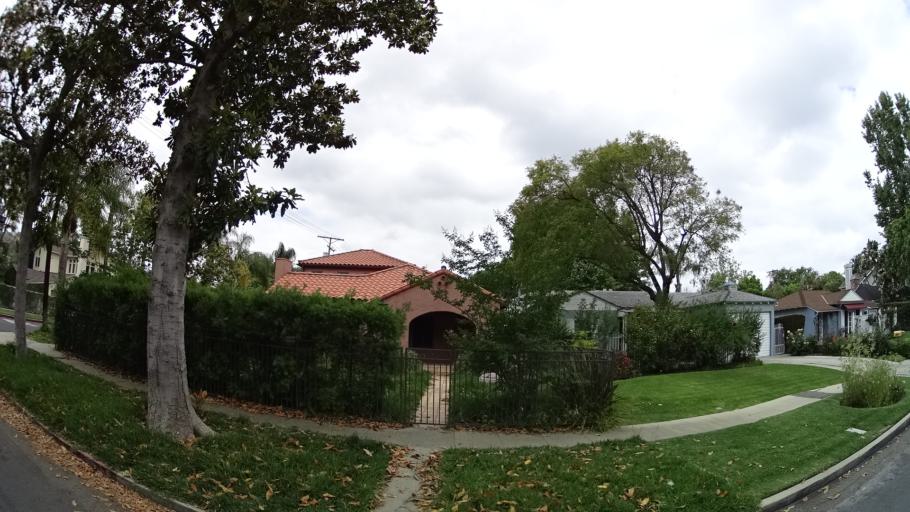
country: US
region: California
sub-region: Los Angeles County
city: North Hollywood
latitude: 34.1469
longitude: -118.3987
